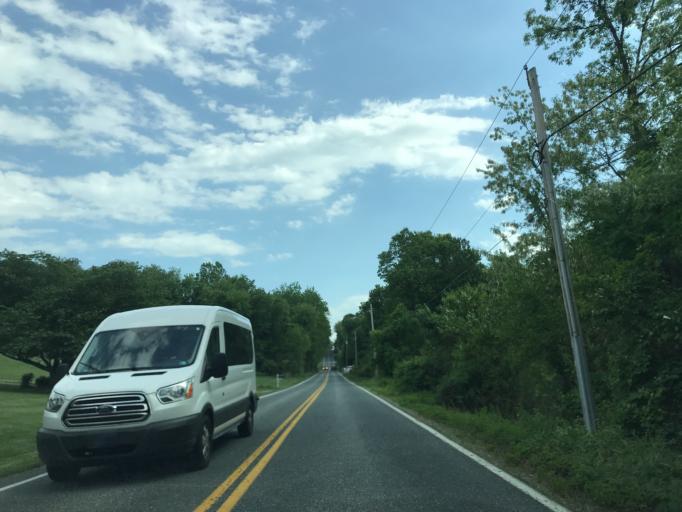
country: US
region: Pennsylvania
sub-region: York County
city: Susquehanna Trails
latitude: 39.6717
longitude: -76.3832
